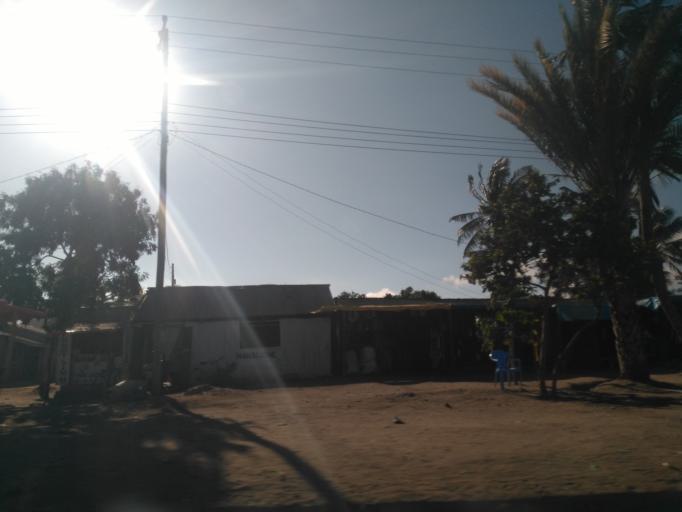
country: TZ
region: Dodoma
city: Dodoma
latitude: -6.1550
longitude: 35.7472
